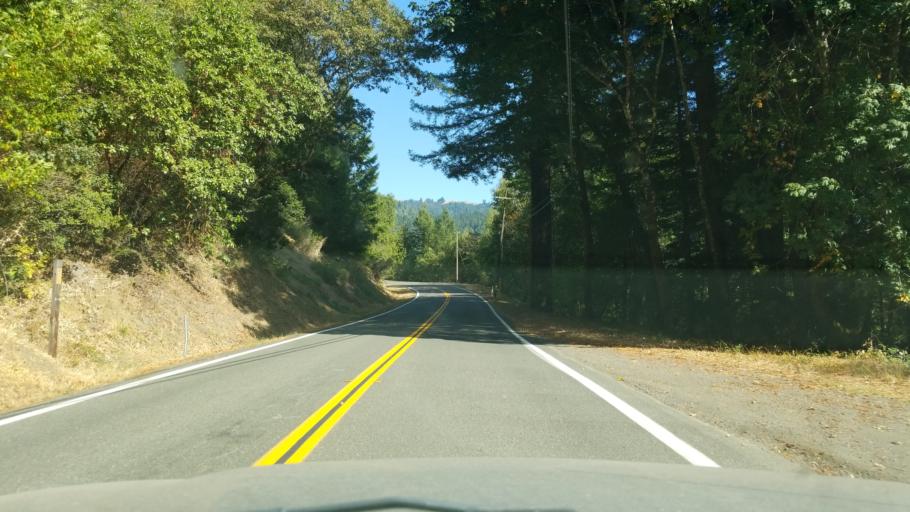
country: US
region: California
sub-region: Humboldt County
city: Redway
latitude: 40.2220
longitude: -123.7977
